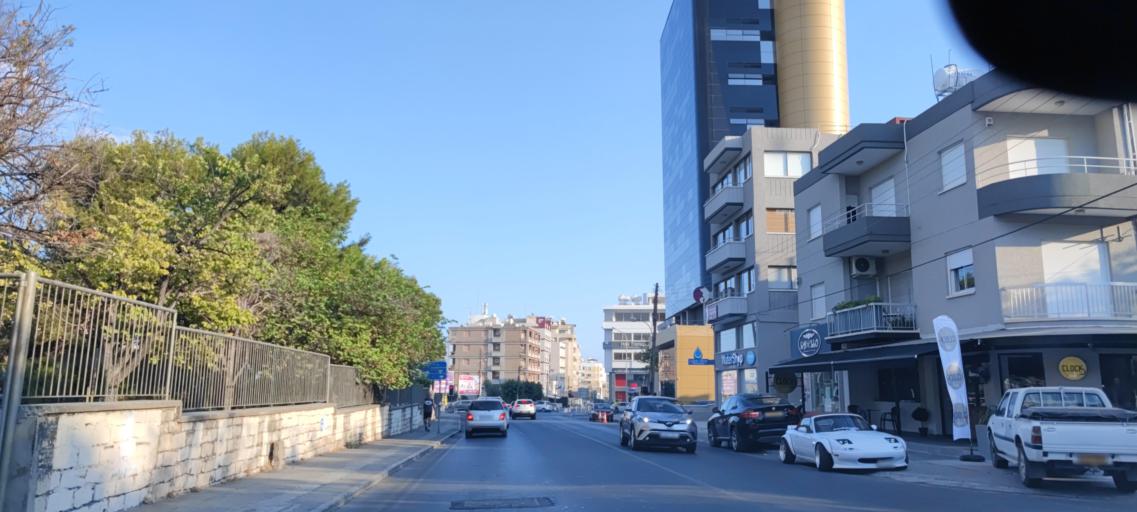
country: CY
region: Limassol
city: Limassol
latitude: 34.6877
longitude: 33.0372
